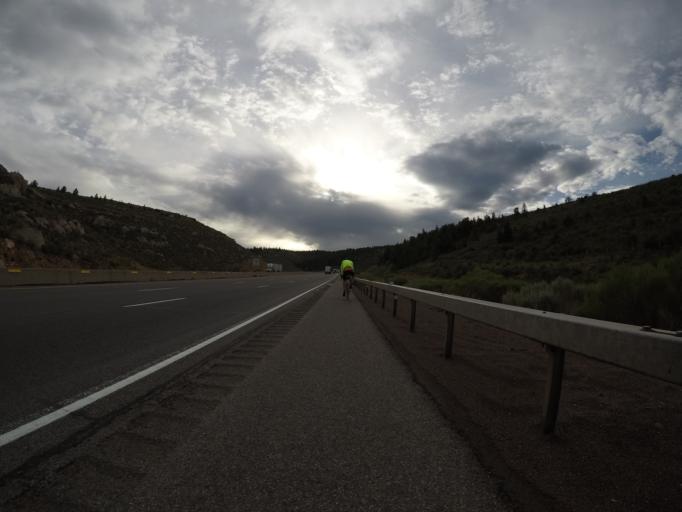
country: US
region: Wyoming
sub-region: Albany County
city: Laramie
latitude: 41.2718
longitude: -105.4891
